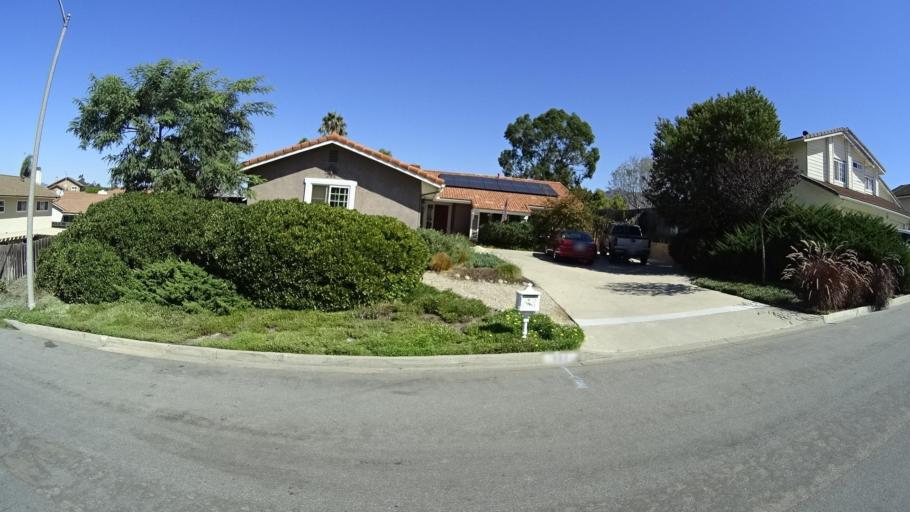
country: US
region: California
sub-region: San Diego County
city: Bonita
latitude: 32.6730
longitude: -117.0019
